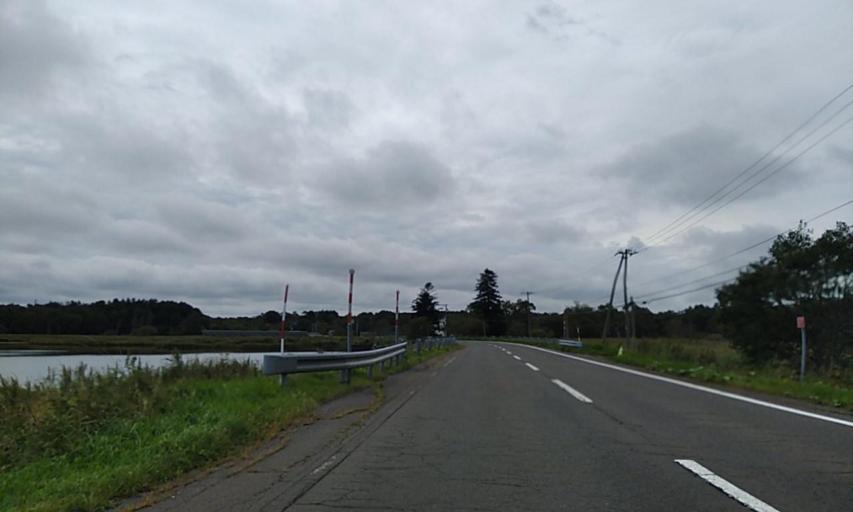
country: JP
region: Hokkaido
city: Shibetsu
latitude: 43.5263
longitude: 145.2384
